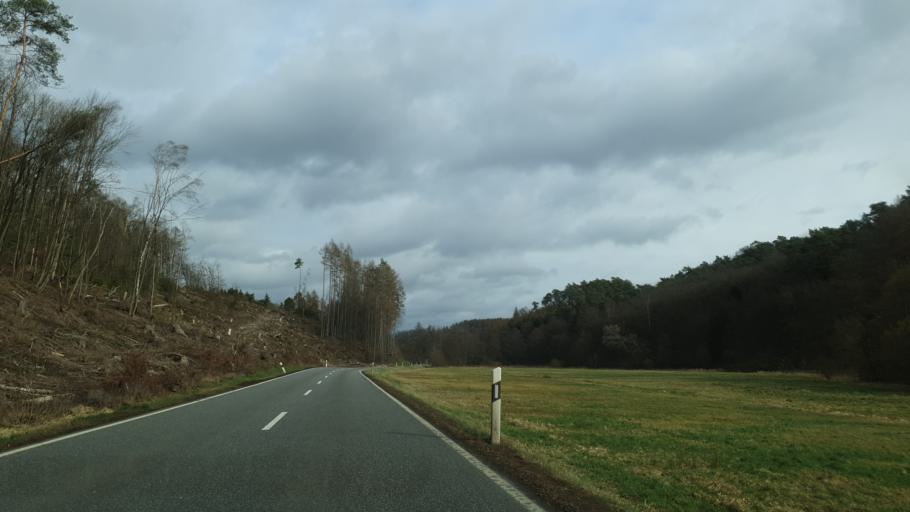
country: DE
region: Rheinland-Pfalz
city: Seifen
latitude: 50.6252
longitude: 7.5750
